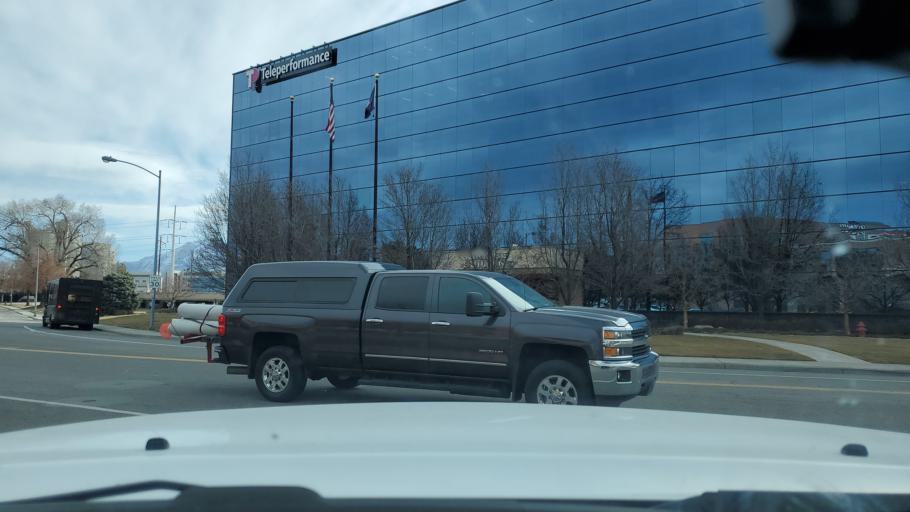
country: US
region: Utah
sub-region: Salt Lake County
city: Murray
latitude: 40.6557
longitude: -111.9001
